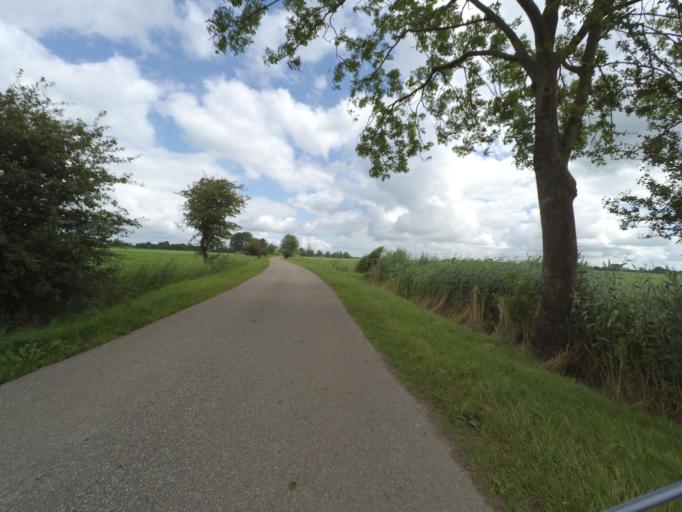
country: NL
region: Friesland
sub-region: Gemeente Kollumerland en Nieuwkruisland
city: Kollum
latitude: 53.2665
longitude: 6.1749
